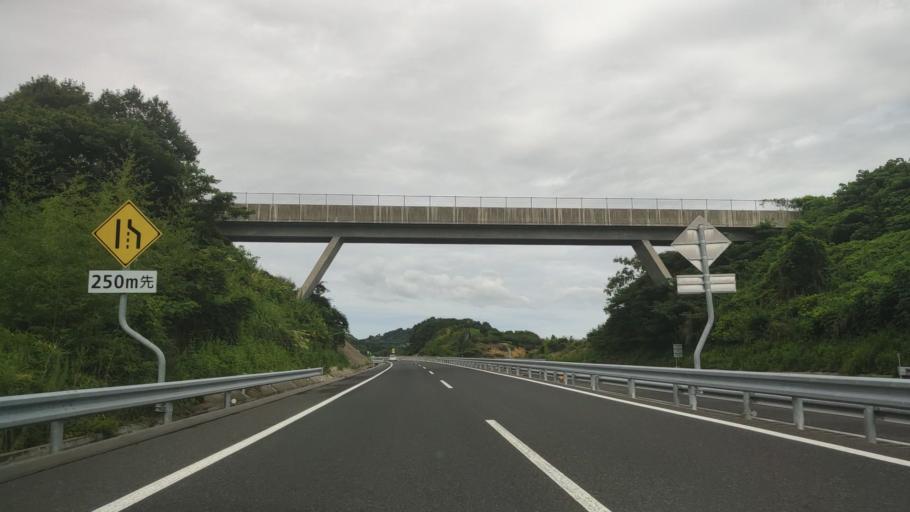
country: JP
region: Wakayama
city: Tanabe
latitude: 33.7617
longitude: 135.3528
